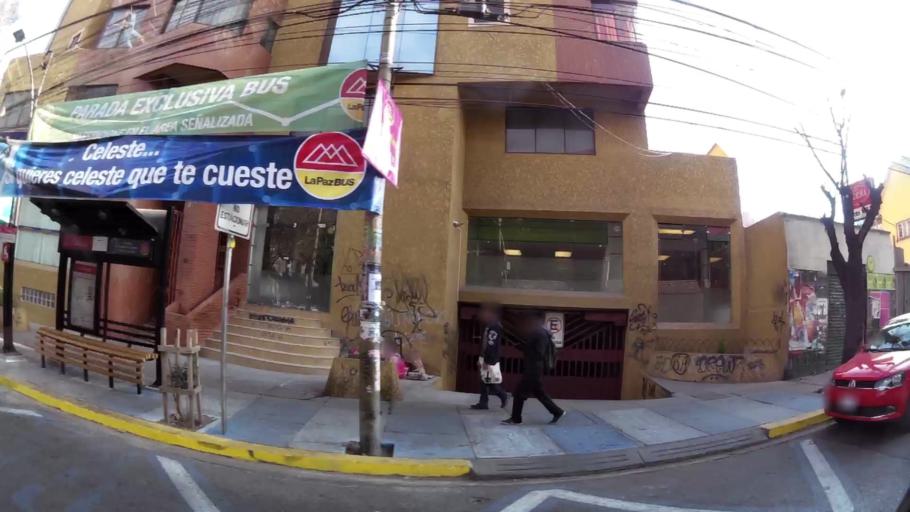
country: BO
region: La Paz
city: La Paz
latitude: -16.4984
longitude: -68.1229
